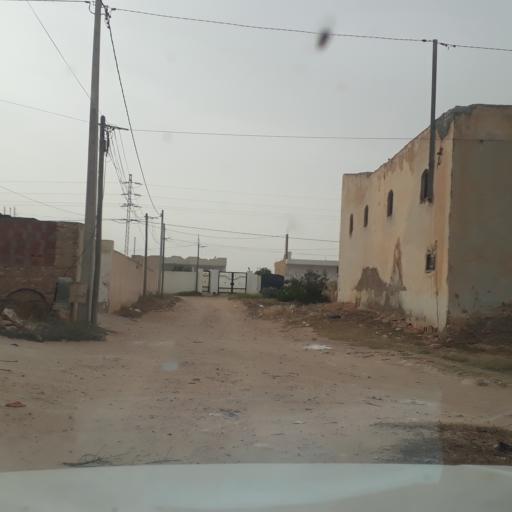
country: TN
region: Safaqis
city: Al Qarmadah
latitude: 34.8286
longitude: 10.7755
